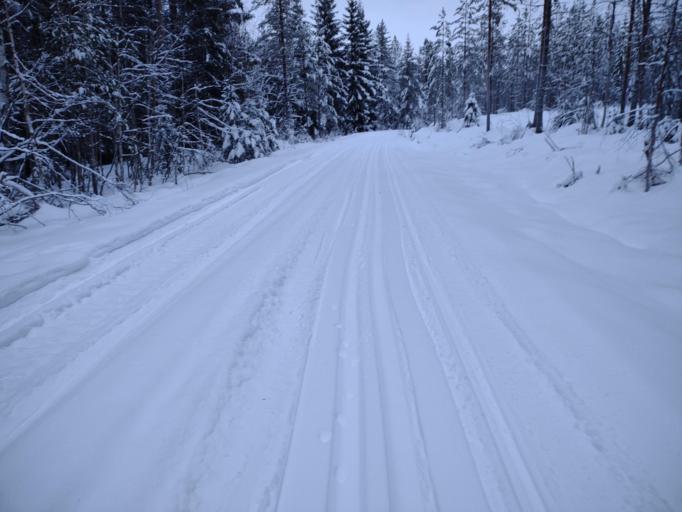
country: NO
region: Buskerud
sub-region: Flesberg
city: Lampeland
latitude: 59.7225
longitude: 9.5443
